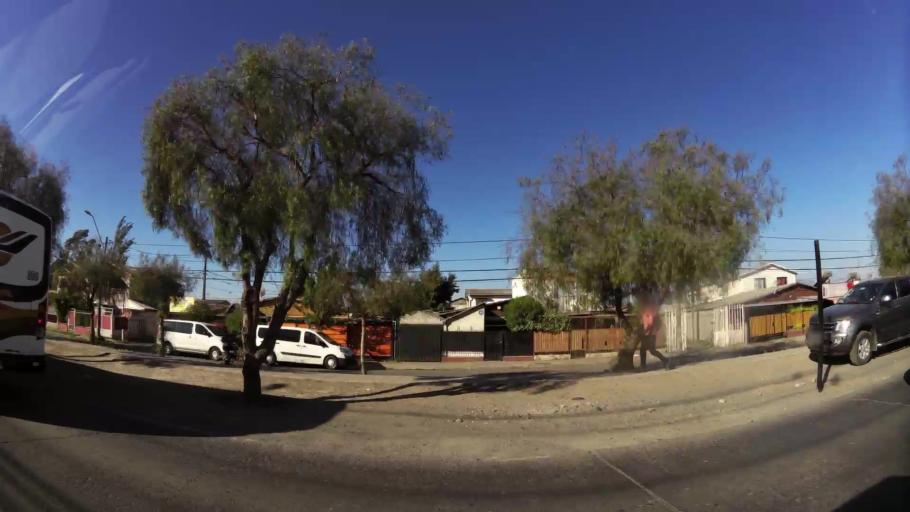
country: CL
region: Santiago Metropolitan
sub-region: Provincia de Maipo
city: San Bernardo
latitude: -33.6036
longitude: -70.6851
